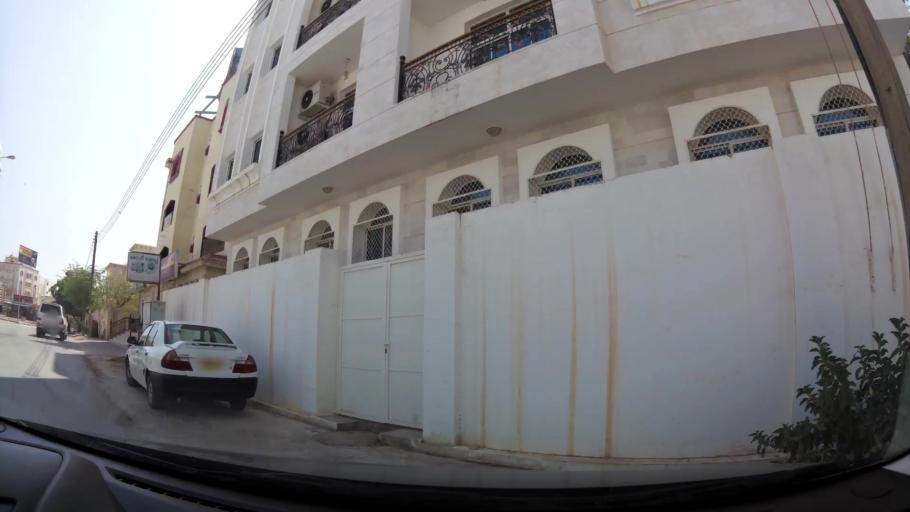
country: OM
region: Zufar
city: Salalah
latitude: 17.0172
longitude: 54.0603
